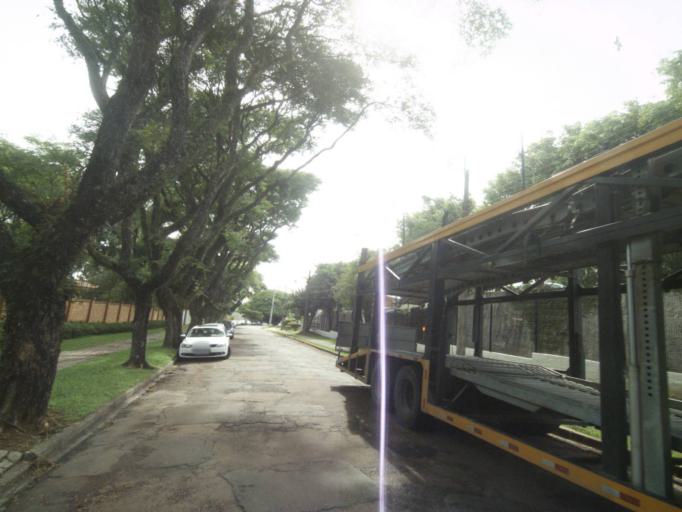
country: BR
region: Parana
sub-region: Curitiba
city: Curitiba
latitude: -25.4401
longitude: -49.3014
